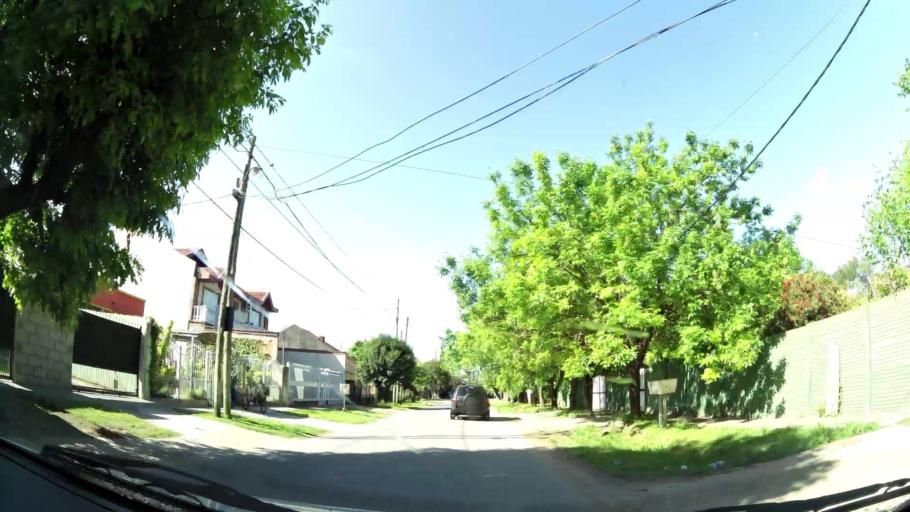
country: AR
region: Buenos Aires
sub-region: Partido de Quilmes
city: Quilmes
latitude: -34.7989
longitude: -58.2325
